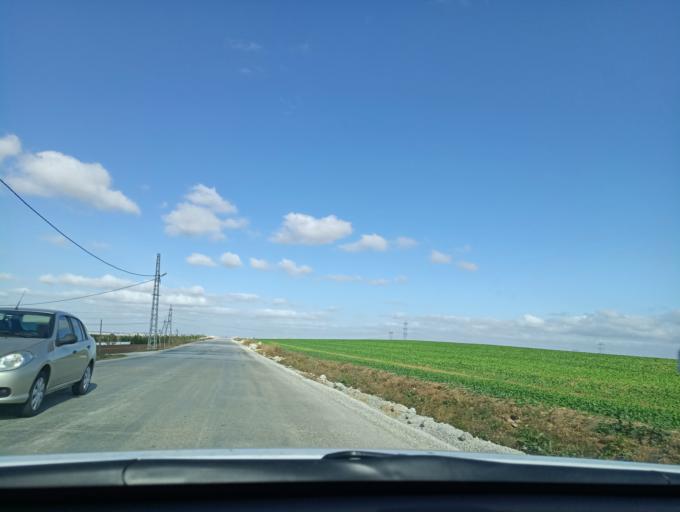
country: TR
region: Tekirdag
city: Corlu
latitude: 41.0532
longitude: 27.8352
